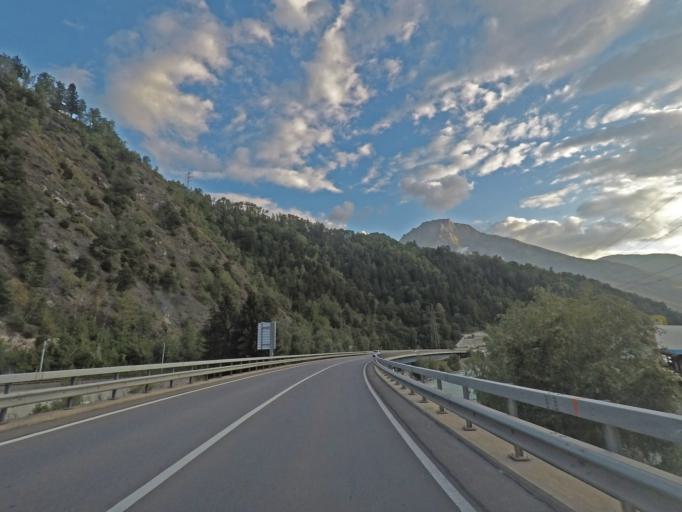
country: CH
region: Valais
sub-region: Brig District
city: Naters
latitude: 46.3284
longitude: 8.0122
